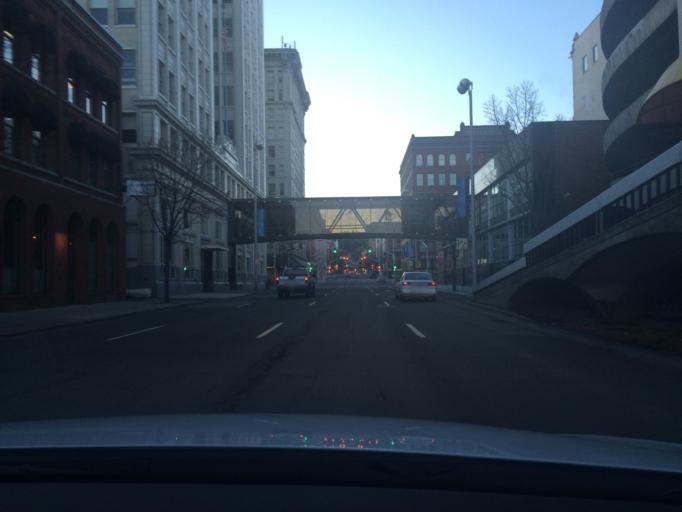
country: US
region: Washington
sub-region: Spokane County
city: Spokane
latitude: 47.6589
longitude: -117.4196
